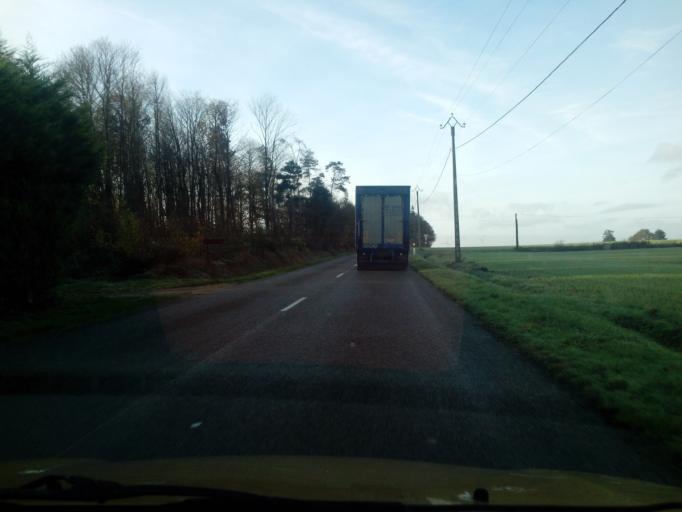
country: FR
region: Brittany
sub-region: Departement du Morbihan
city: Guilliers
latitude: 48.0322
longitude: -2.4240
